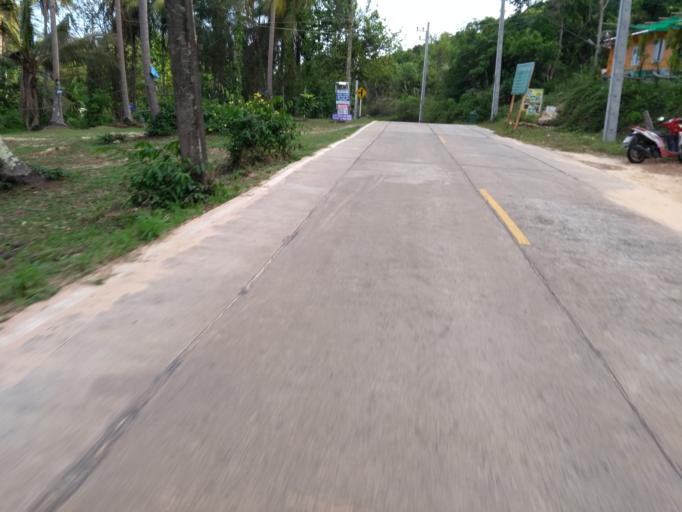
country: TH
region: Trat
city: Ko Kut
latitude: 11.6291
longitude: 102.5463
